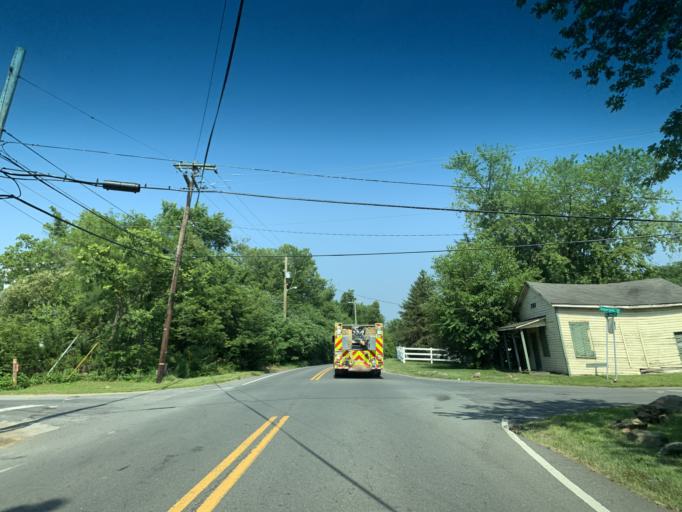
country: US
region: Maryland
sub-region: Montgomery County
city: Darnestown
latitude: 39.1283
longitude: -77.3470
